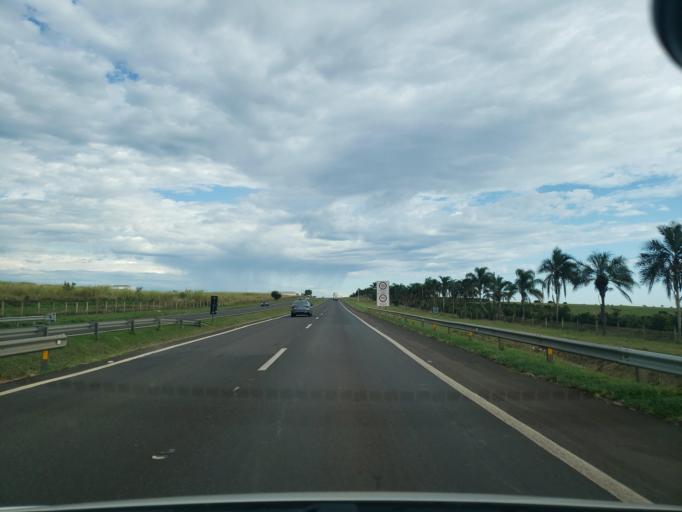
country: BR
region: Sao Paulo
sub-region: Jau
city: Jau
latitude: -22.2673
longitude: -48.5013
